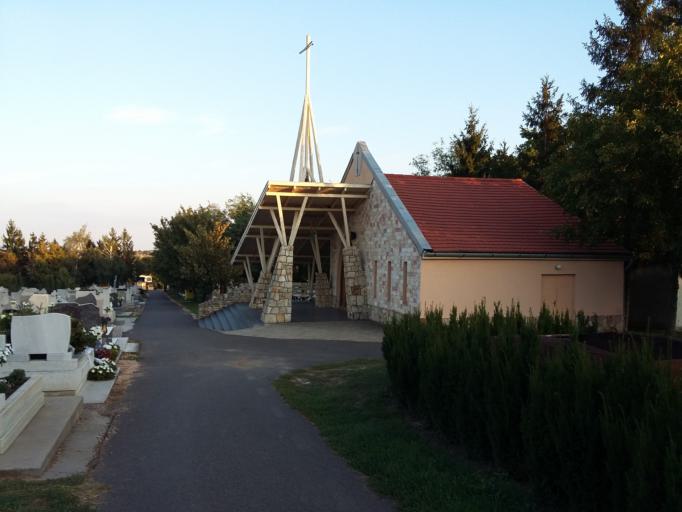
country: HU
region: Borsod-Abauj-Zemplen
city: Bekecs
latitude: 48.1563
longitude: 21.1780
